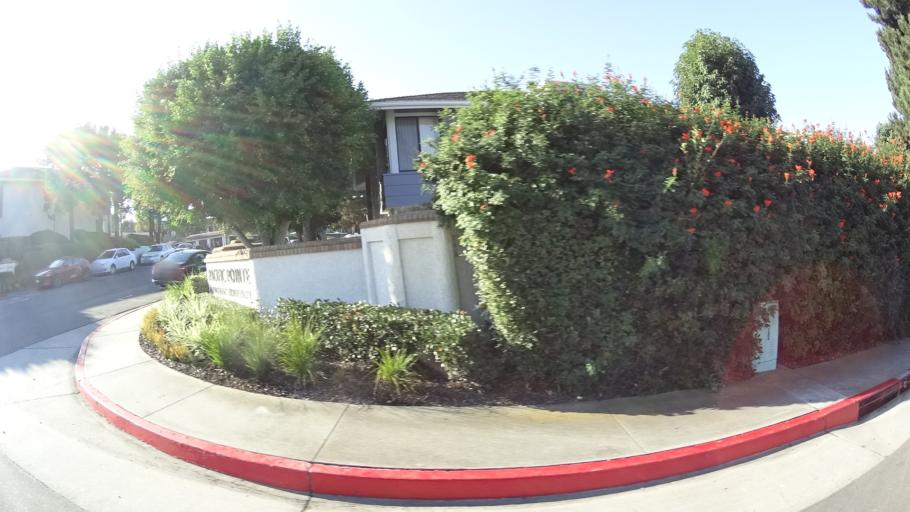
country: US
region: California
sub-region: Orange County
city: San Clemente
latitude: 33.4476
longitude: -117.6309
